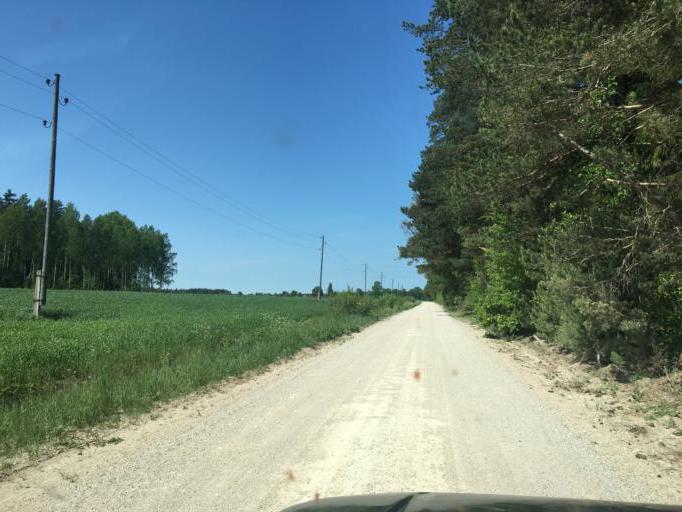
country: LV
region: Talsu Rajons
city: Valdemarpils
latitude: 57.4235
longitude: 22.6957
